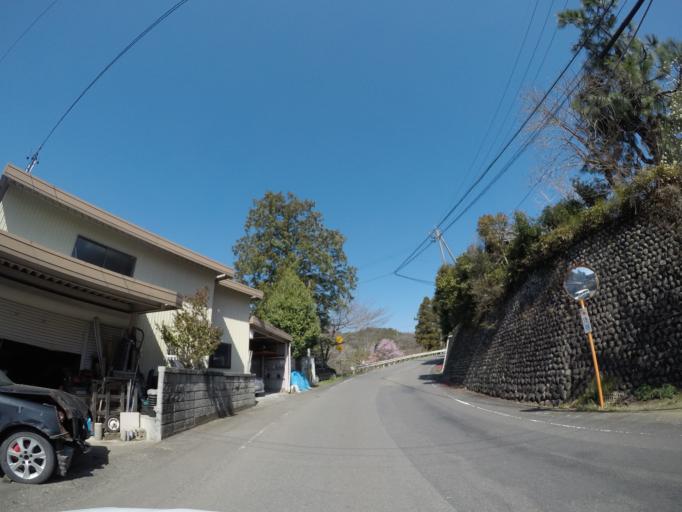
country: JP
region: Shizuoka
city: Kanaya
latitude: 34.7915
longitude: 138.1260
